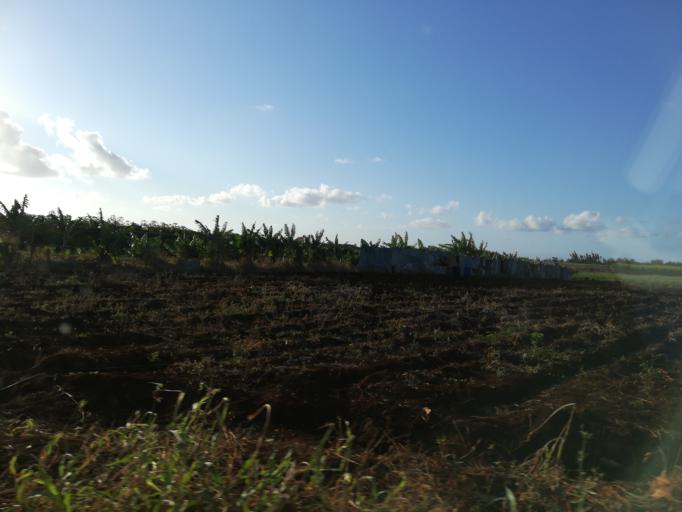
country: MU
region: Pamplemousses
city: Morcellemont Saint Andre
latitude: -20.0799
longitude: 57.5357
